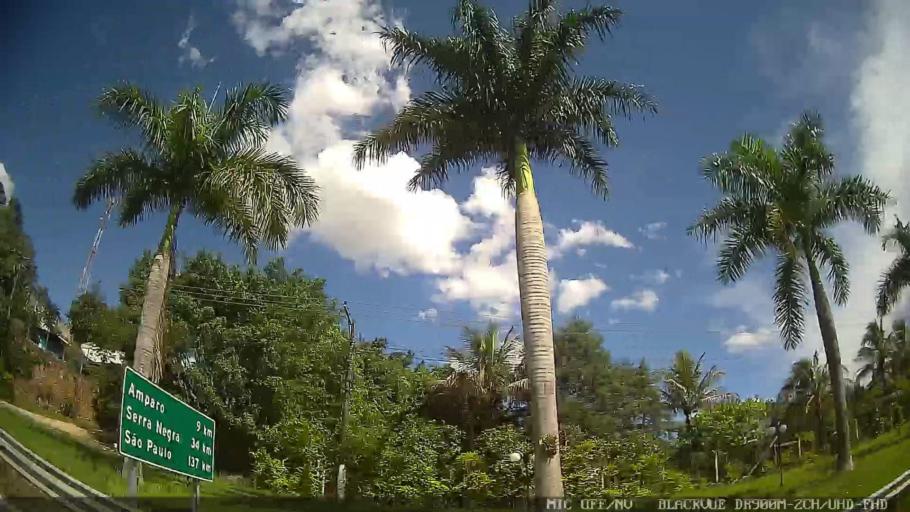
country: BR
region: Sao Paulo
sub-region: Pedreira
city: Pedreira
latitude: -22.7115
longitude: -46.8390
